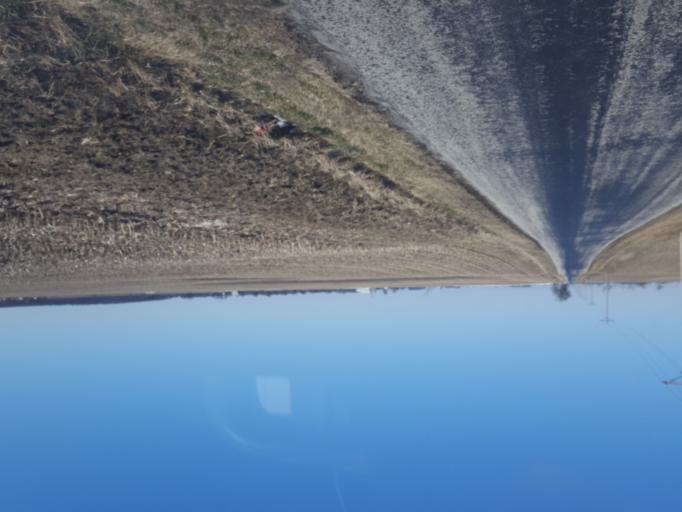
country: US
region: Ohio
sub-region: Marion County
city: Marion
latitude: 40.6458
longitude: -83.1980
